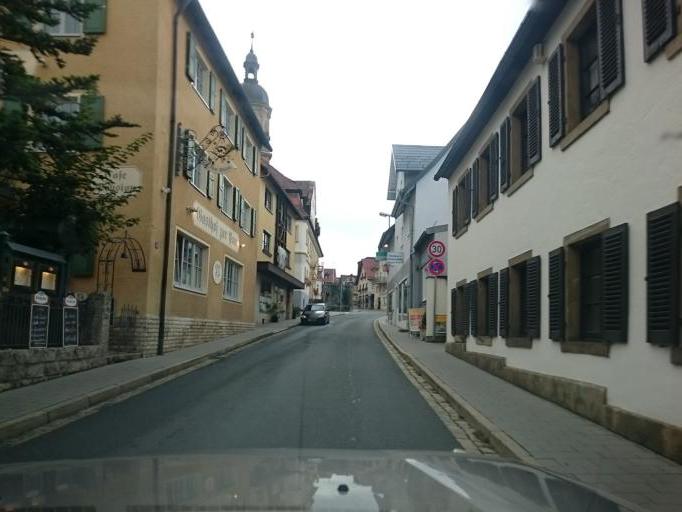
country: DE
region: Bavaria
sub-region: Upper Franconia
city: Gossweinstein
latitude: 49.7707
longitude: 11.3380
